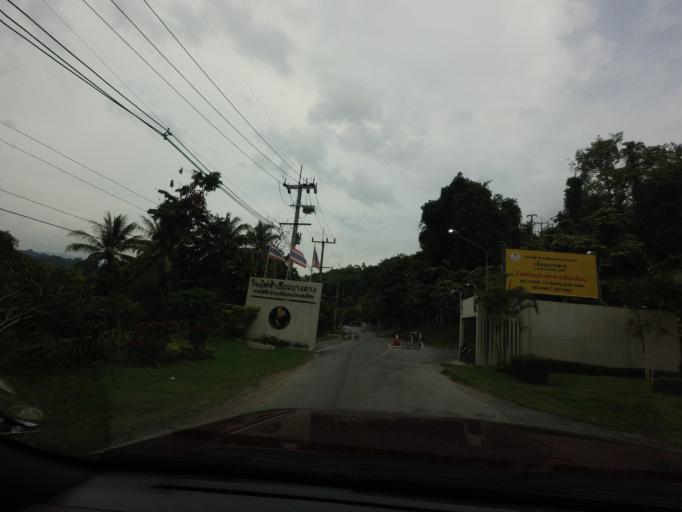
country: TH
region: Yala
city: Than To
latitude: 6.1626
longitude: 101.2690
